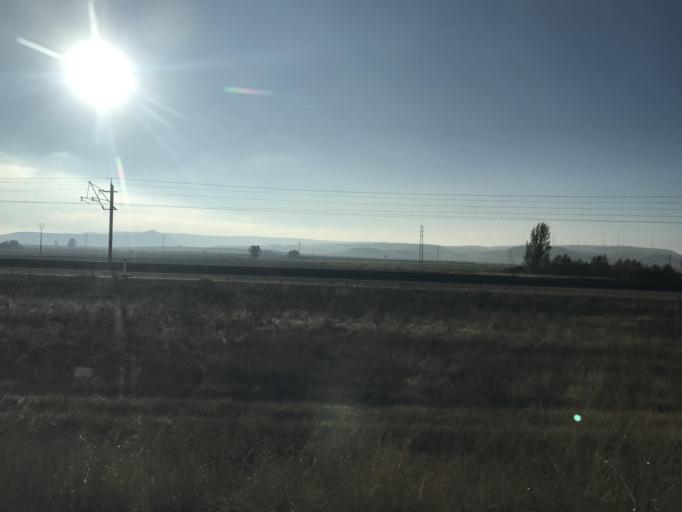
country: ES
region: Castille and Leon
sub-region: Provincia de Palencia
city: Quintana del Puente
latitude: 42.0756
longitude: -4.2054
